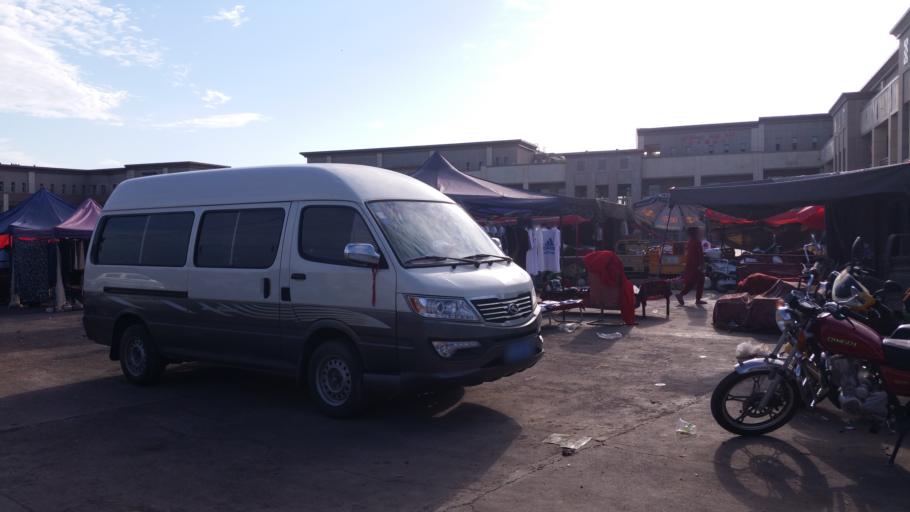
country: CN
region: Xinjiang Uygur Zizhiqu
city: Laochenglu
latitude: 42.9406
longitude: 89.1721
